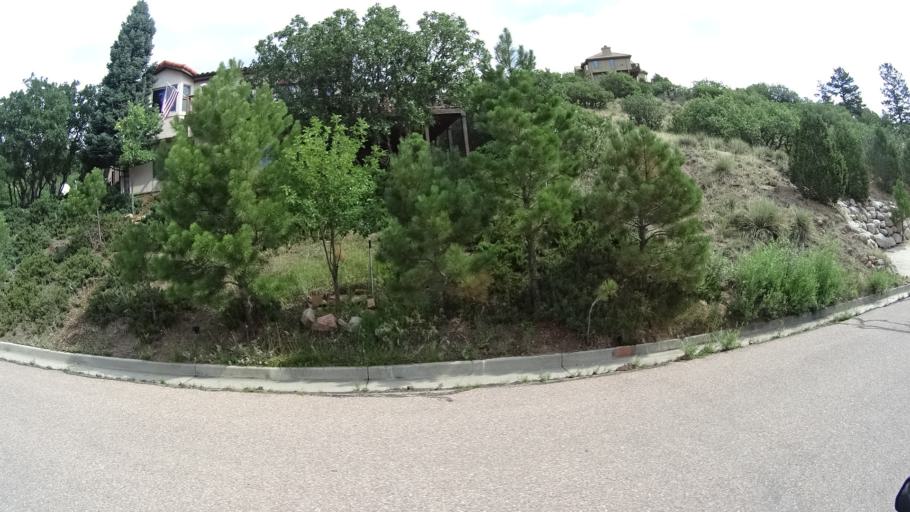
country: US
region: Colorado
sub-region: El Paso County
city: Air Force Academy
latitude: 38.9520
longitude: -104.8695
